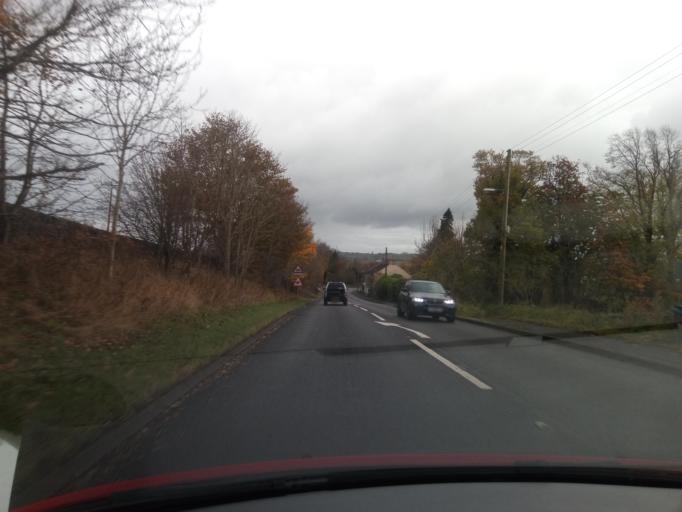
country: GB
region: England
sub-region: County Durham
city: Hamsterley
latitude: 54.6812
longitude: -1.7825
